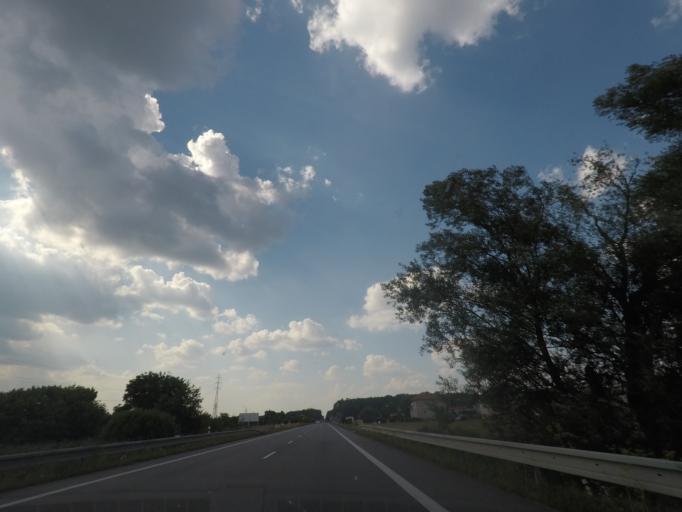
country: CZ
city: Albrechtice nad Orlici
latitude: 50.1706
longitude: 16.0400
